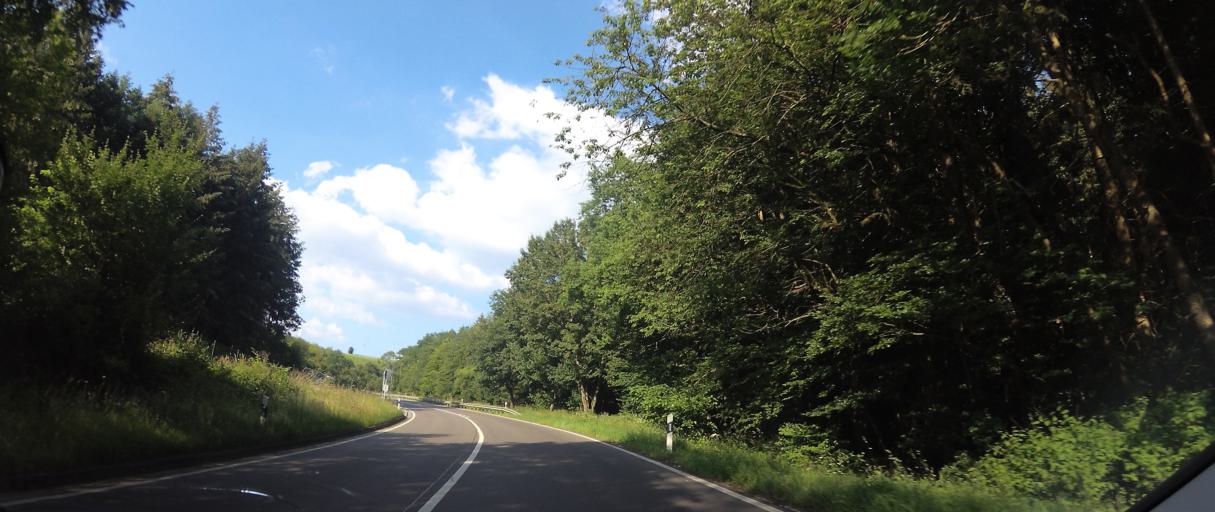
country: DE
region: Rheinland-Pfalz
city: Hochstatten
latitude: 49.7615
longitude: 7.8405
